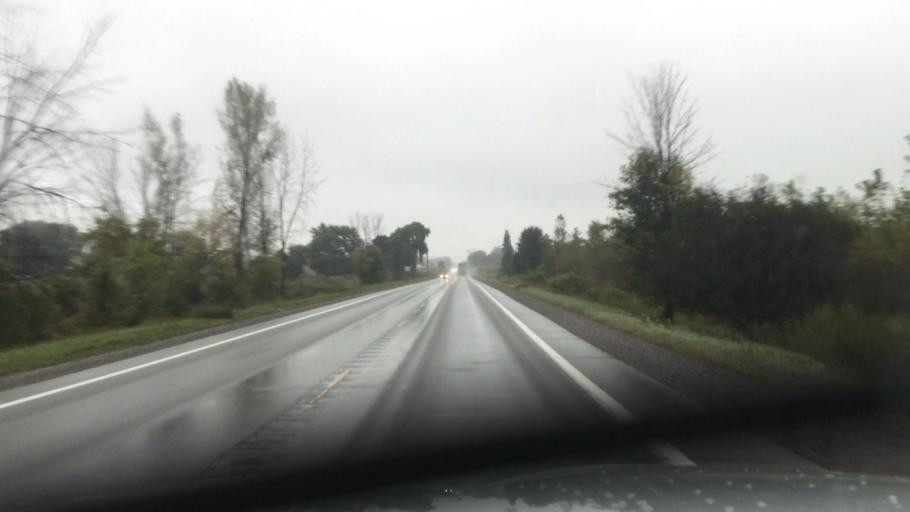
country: US
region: Michigan
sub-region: Saginaw County
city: Saginaw
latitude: 43.3614
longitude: -83.9548
